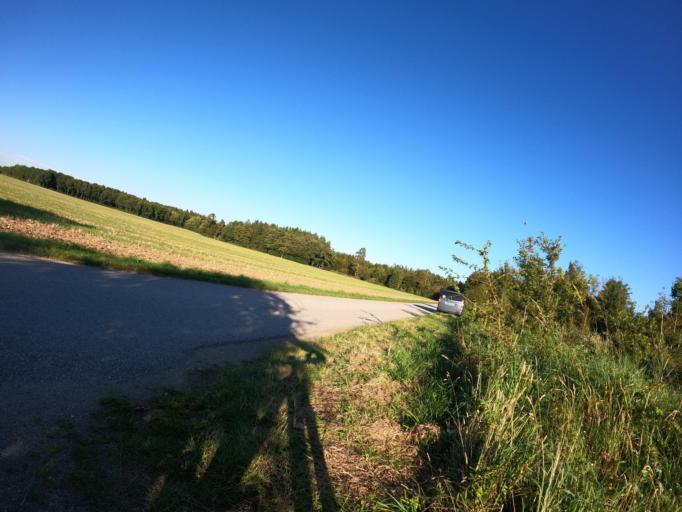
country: DE
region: Bavaria
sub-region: Upper Bavaria
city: Oberpframmern
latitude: 48.0556
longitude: 11.7835
